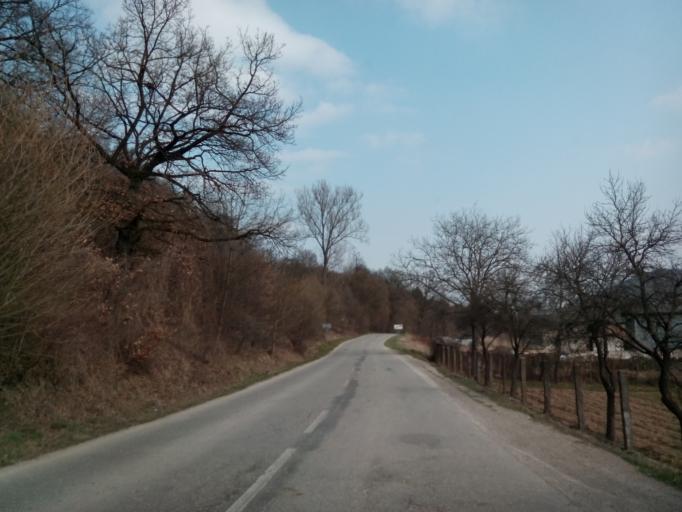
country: SK
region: Trenciansky
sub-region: Okres Trencin
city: Trencin
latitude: 48.9681
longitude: 17.9894
